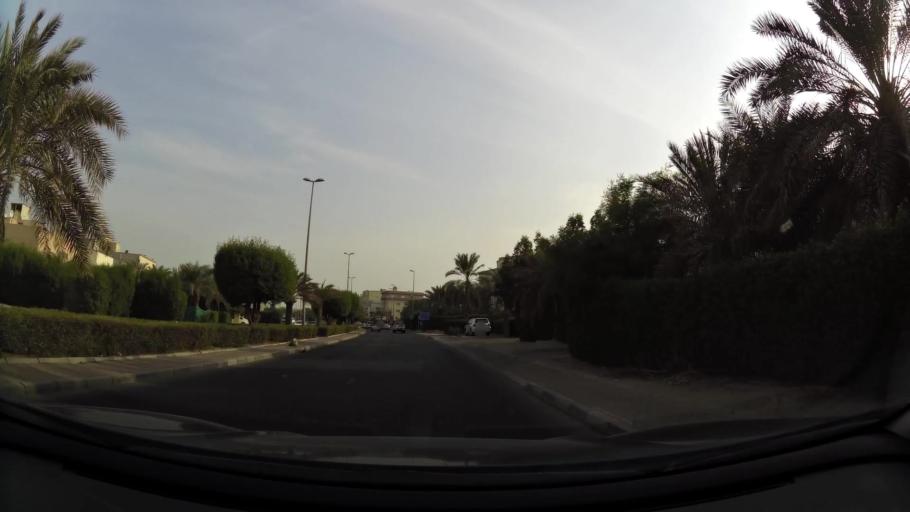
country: KW
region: Mubarak al Kabir
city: Mubarak al Kabir
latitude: 29.2180
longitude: 48.0622
